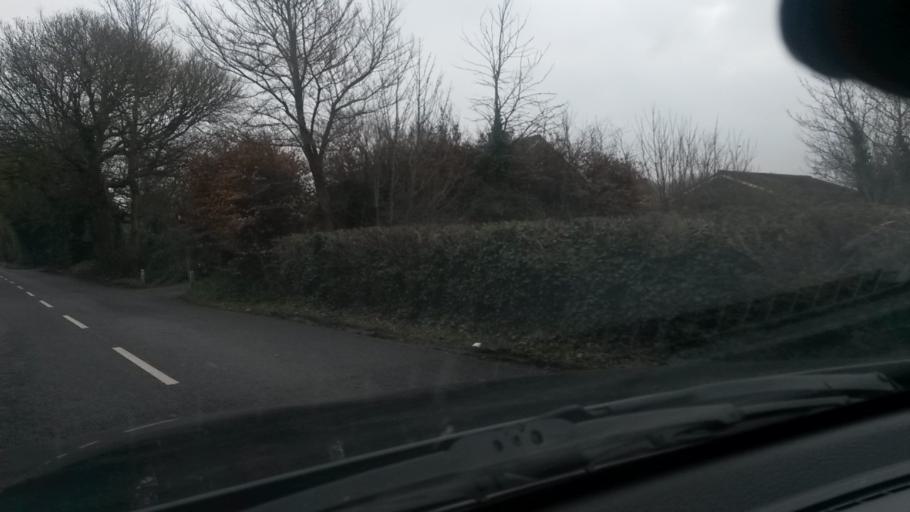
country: IE
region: Leinster
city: Kinsealy-Drinan
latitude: 53.4249
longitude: -6.2050
